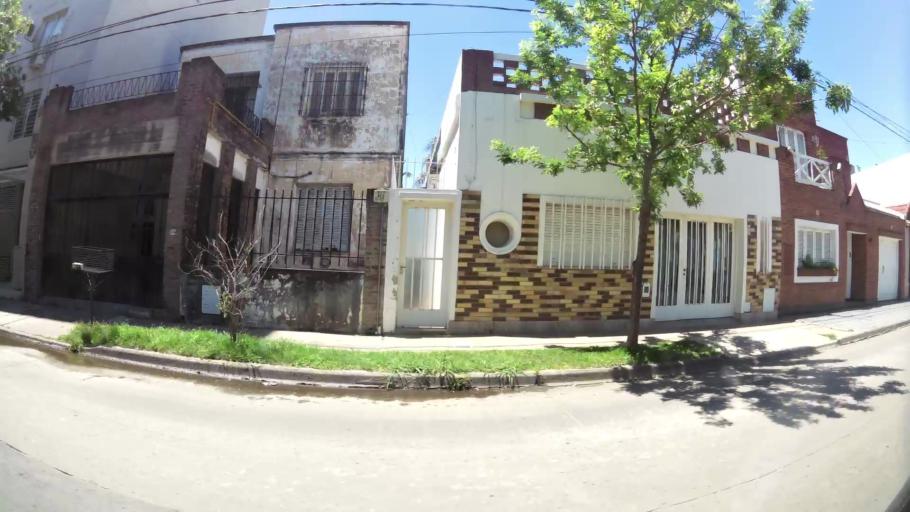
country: AR
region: Santa Fe
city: Santa Fe de la Vera Cruz
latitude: -31.6332
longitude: -60.7095
